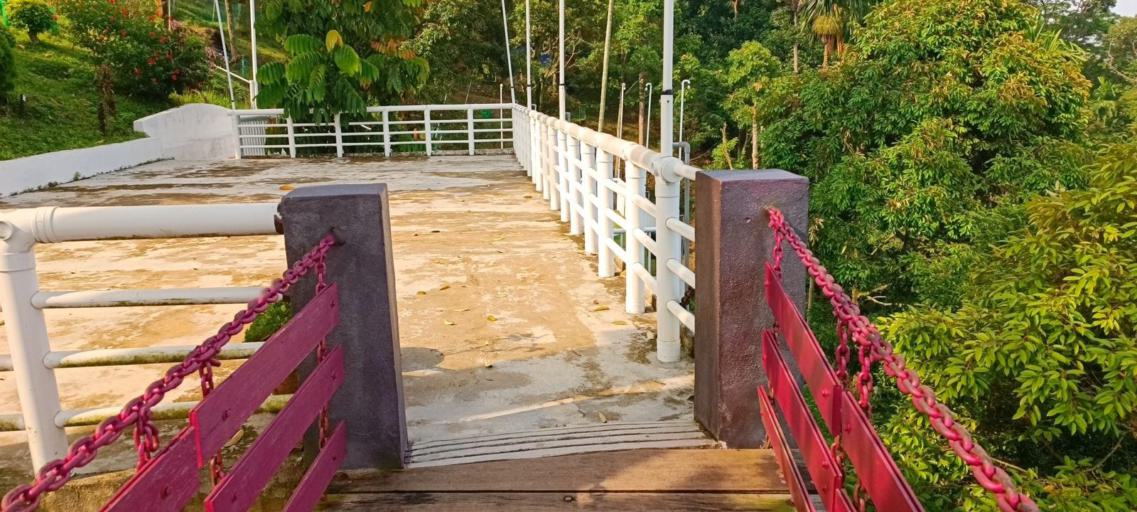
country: MY
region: Penang
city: Bukit Mertajam
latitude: 5.4084
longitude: 100.5079
